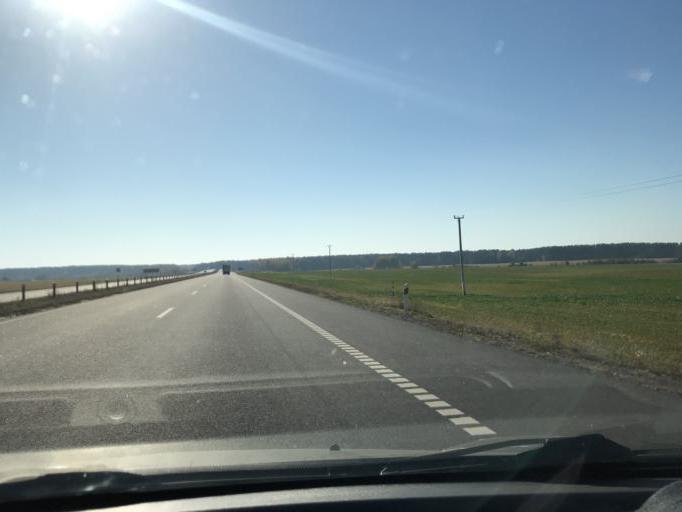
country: BY
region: Mogilev
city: Babruysk
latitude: 53.1684
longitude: 29.3600
